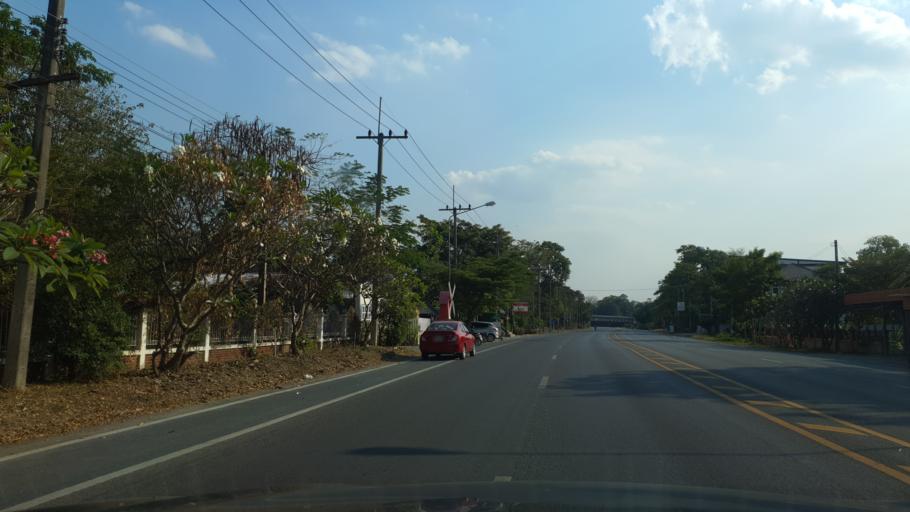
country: TH
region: Tak
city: Tak
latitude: 16.8599
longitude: 99.1215
